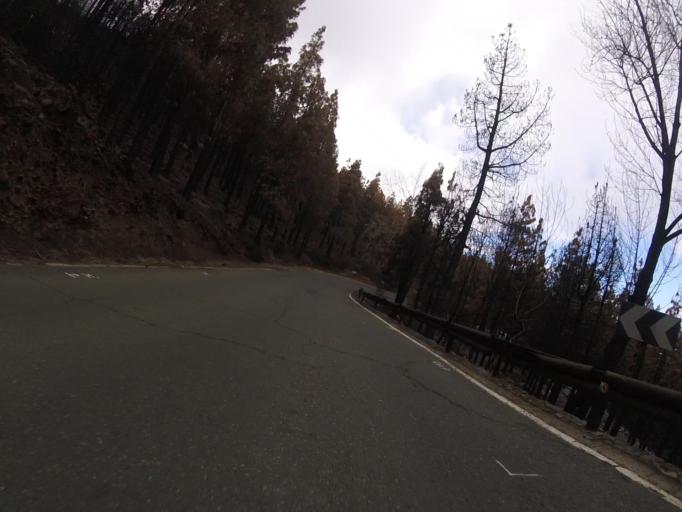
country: ES
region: Canary Islands
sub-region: Provincia de Las Palmas
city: Tejeda
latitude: 27.9859
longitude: -15.5804
